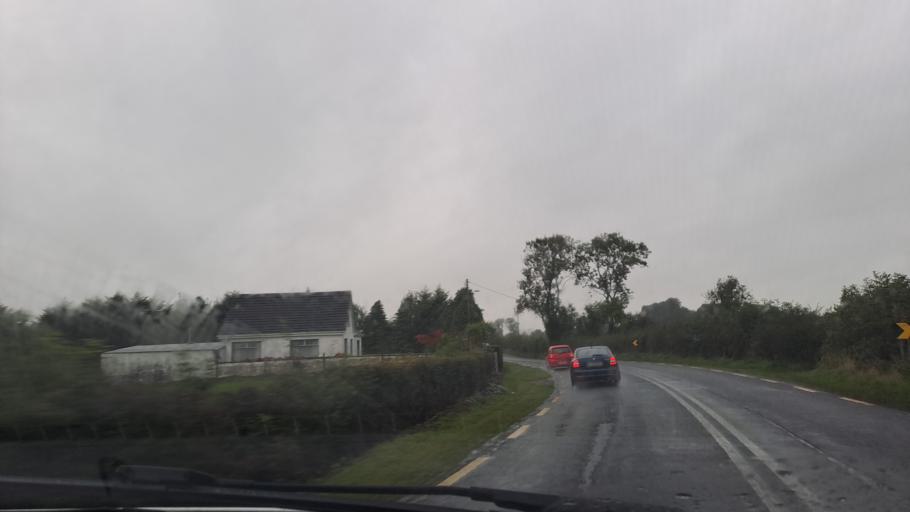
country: IE
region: Leinster
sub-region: Lu
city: Dundalk
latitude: 53.9893
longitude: -6.4769
